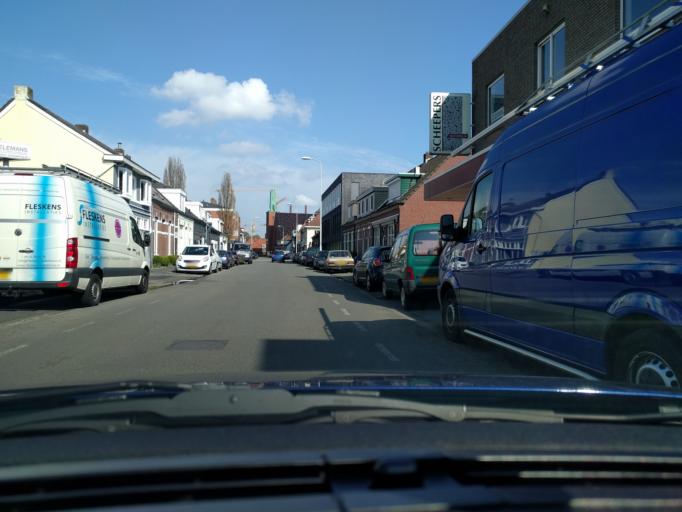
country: NL
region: North Brabant
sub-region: Gemeente Eindhoven
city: Eindhoven
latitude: 51.4424
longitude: 5.4556
